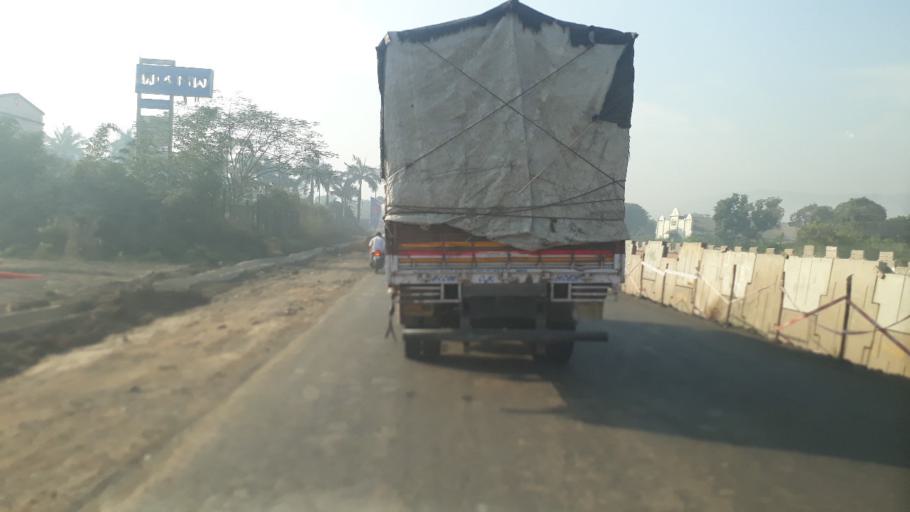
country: IN
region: Maharashtra
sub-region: Raigarh
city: Kalundri
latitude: 18.9296
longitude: 73.1273
